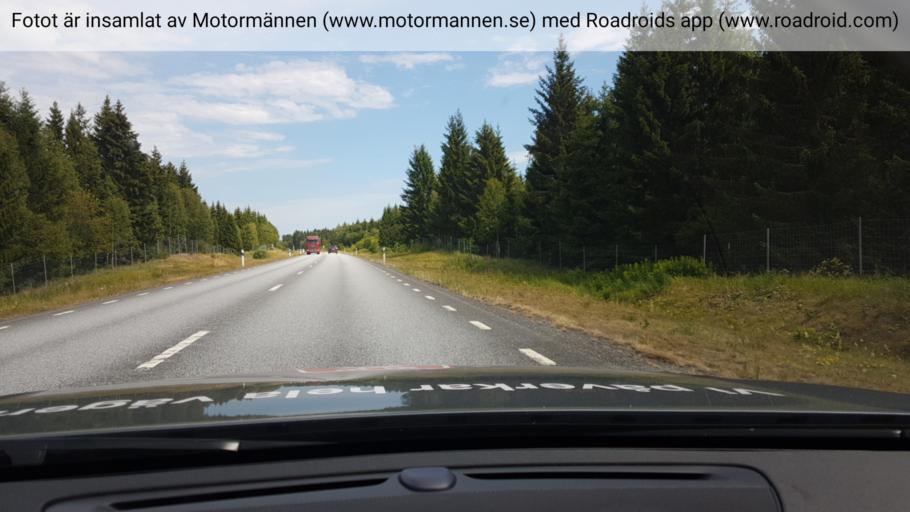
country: SE
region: Uppsala
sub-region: Osthammars Kommun
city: OEsthammar
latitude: 60.1725
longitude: 18.3244
